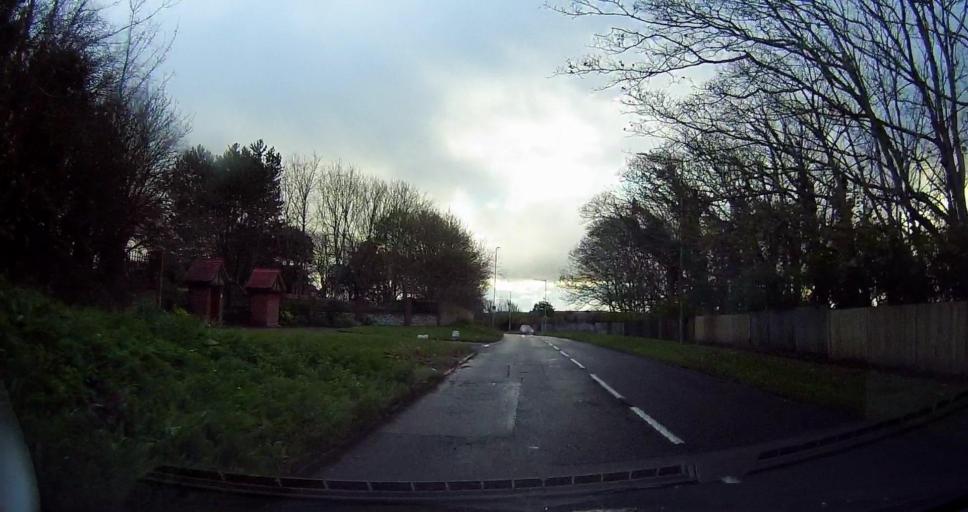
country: GB
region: England
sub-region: Brighton and Hove
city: Rottingdean
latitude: 50.8176
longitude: -0.0644
